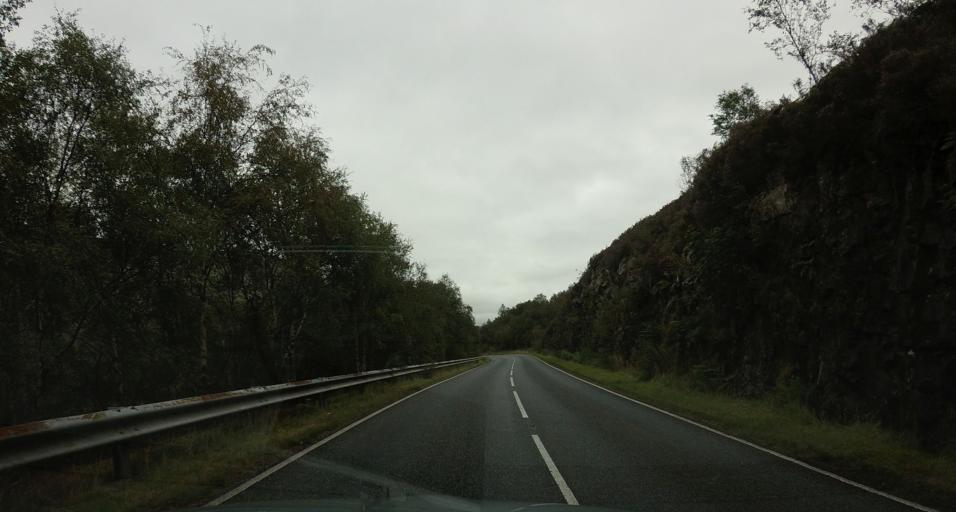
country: GB
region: Scotland
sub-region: Highland
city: Fort William
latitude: 56.6979
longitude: -5.0706
